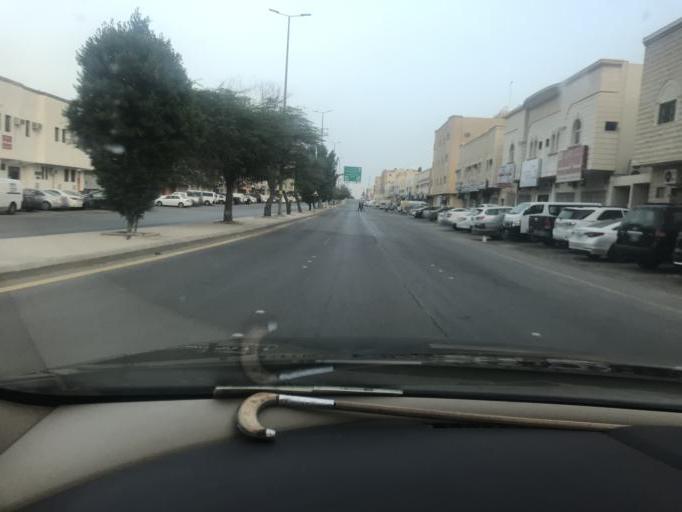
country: SA
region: Ar Riyad
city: Riyadh
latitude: 24.7302
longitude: 46.7628
